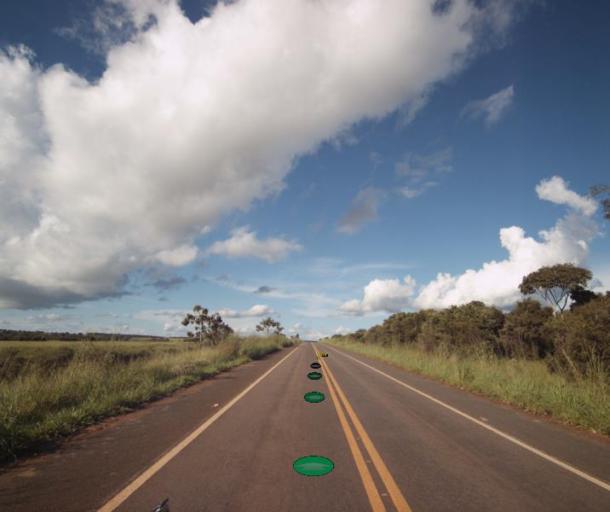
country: BR
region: Goias
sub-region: Itaberai
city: Itaberai
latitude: -15.9959
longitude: -49.7380
